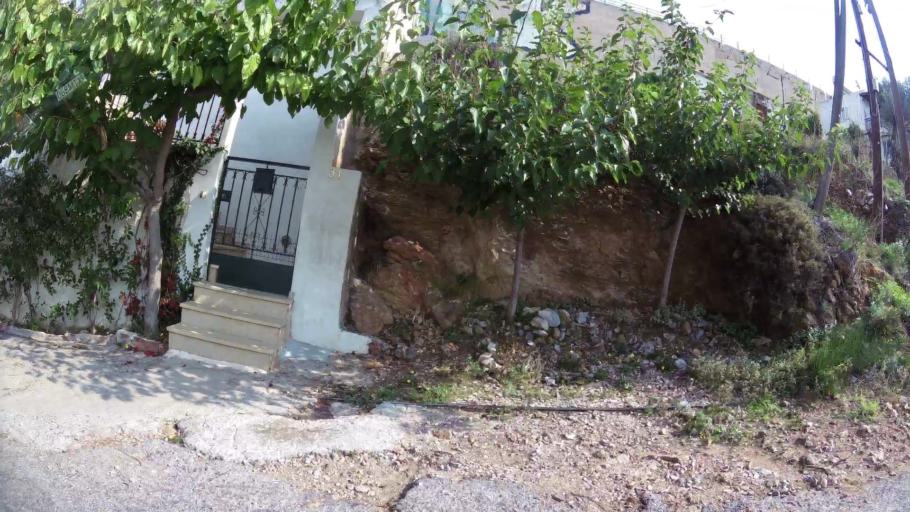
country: GR
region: Attica
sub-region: Nomarchia Athinas
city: Galatsi
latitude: 38.0061
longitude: 23.7538
